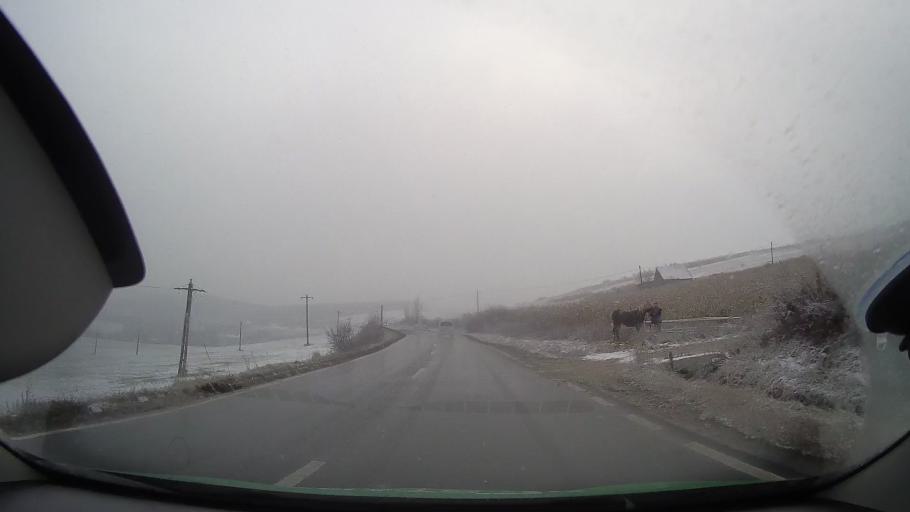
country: RO
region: Mures
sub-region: Comuna Bagaciu
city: Delenii
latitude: 46.2653
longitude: 24.3003
